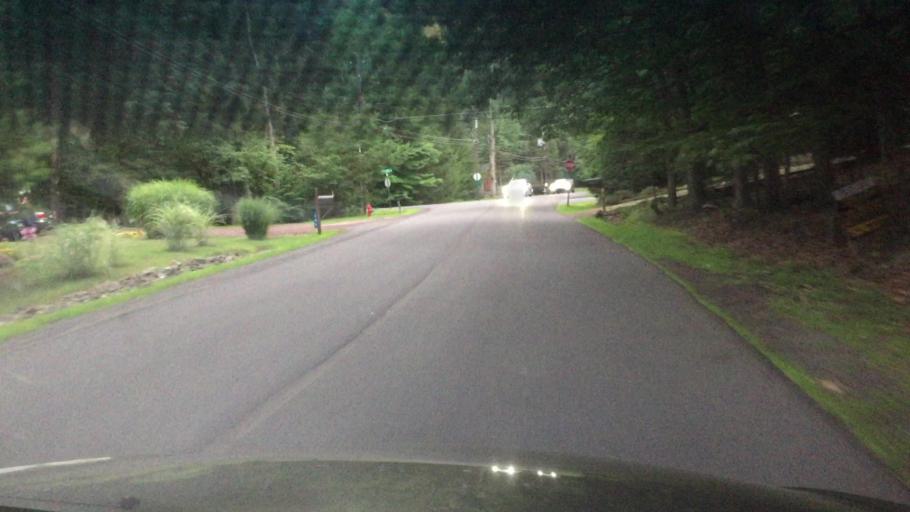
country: US
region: Pennsylvania
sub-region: Luzerne County
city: Freeland
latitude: 41.0400
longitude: -75.9379
